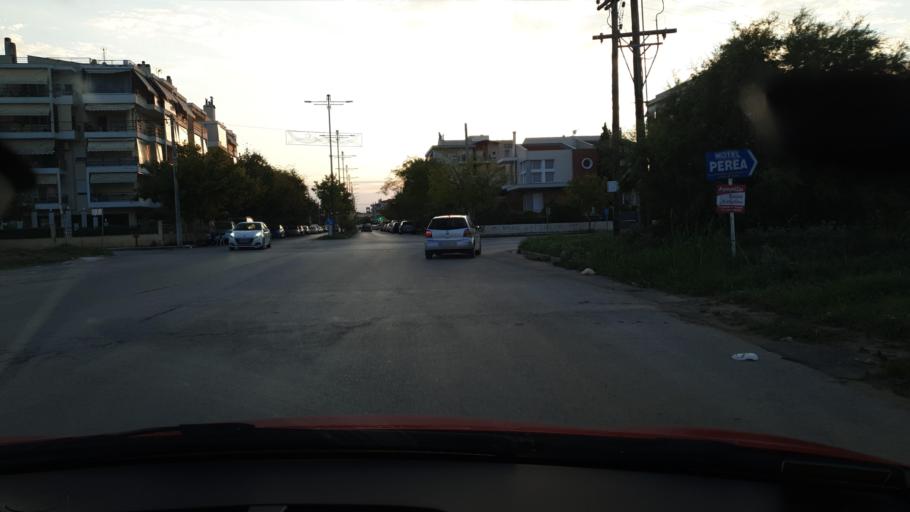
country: GR
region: Central Macedonia
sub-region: Nomos Thessalonikis
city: Peraia
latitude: 40.5080
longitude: 22.9375
